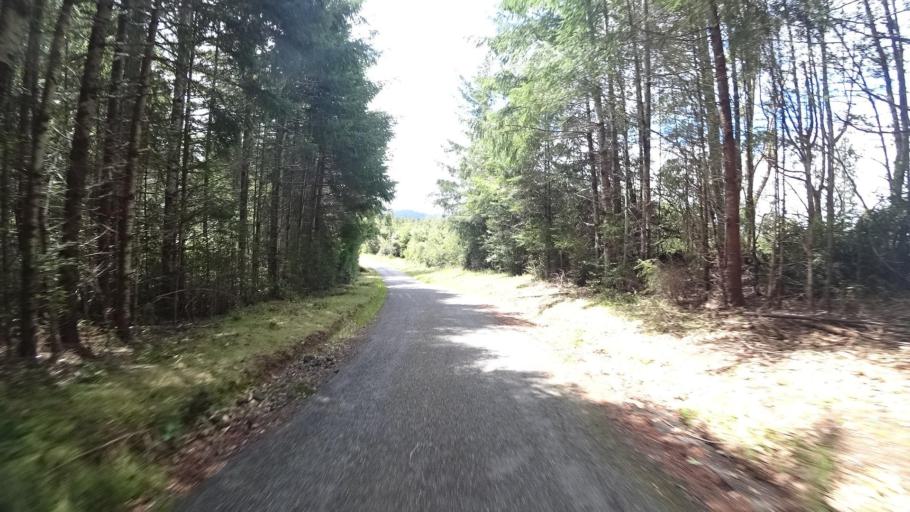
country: US
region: California
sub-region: Humboldt County
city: Blue Lake
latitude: 40.7817
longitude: -123.9627
